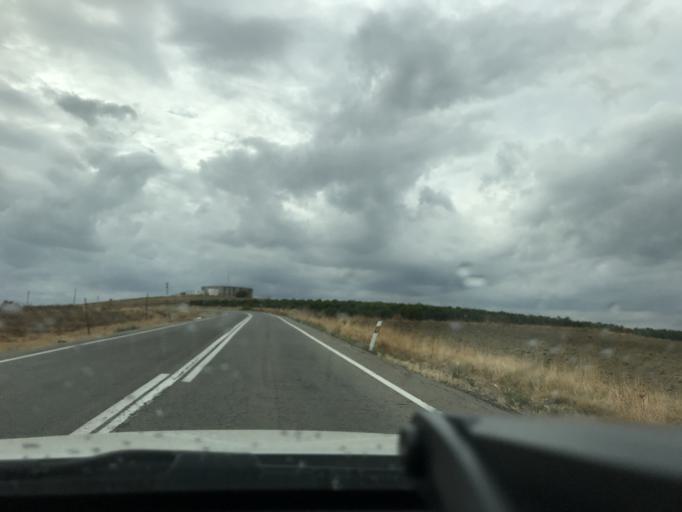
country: ES
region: Andalusia
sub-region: Provincia de Sevilla
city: Cantillana
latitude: 37.6160
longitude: -5.8008
